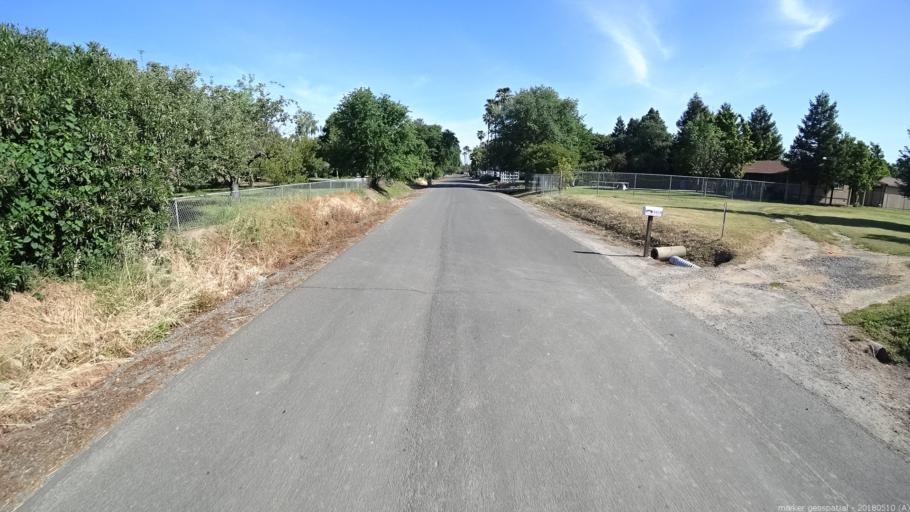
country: US
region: California
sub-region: Sacramento County
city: Rio Linda
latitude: 38.6607
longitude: -121.4785
